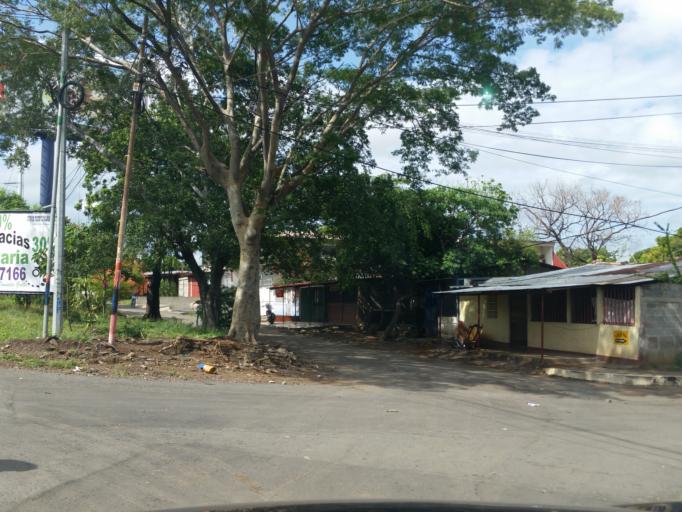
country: NI
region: Managua
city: Managua
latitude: 12.1317
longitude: -86.2309
